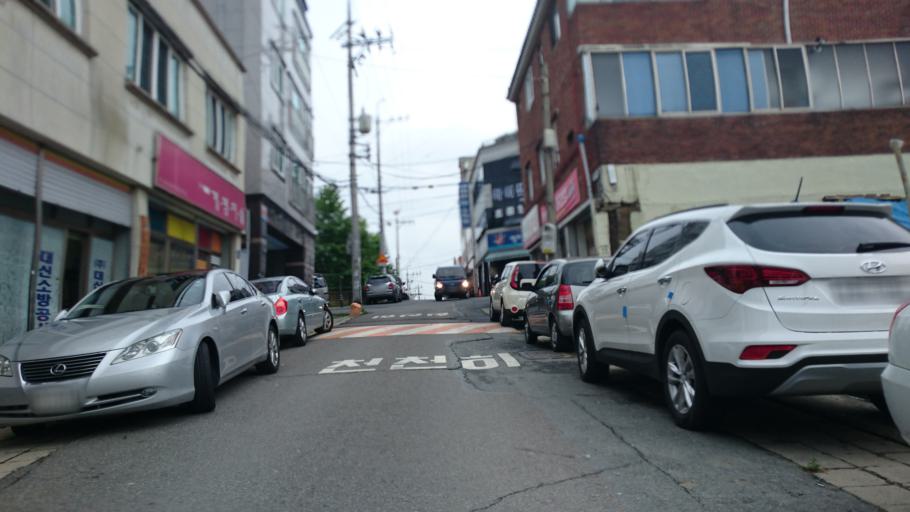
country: KR
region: Daegu
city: Daegu
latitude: 35.8661
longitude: 128.6472
